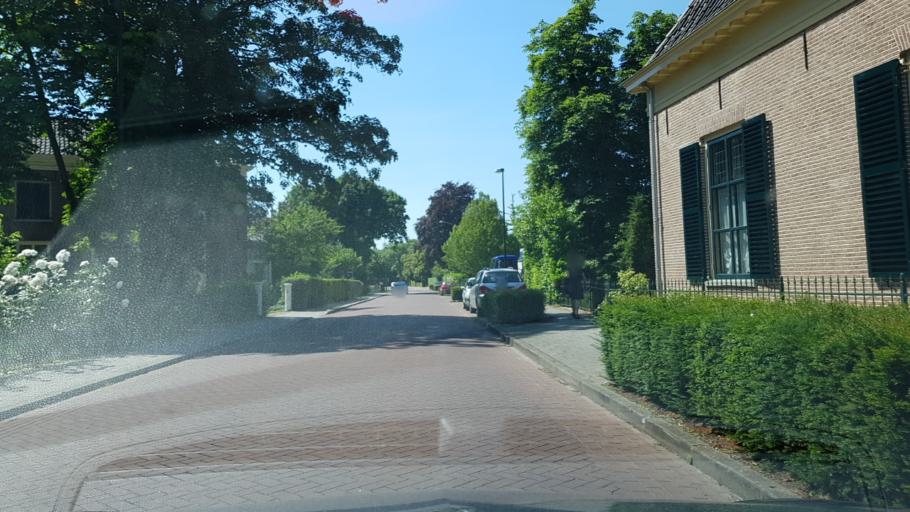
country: NL
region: Gelderland
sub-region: Gemeente Brummen
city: Brummen
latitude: 52.0847
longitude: 6.1543
